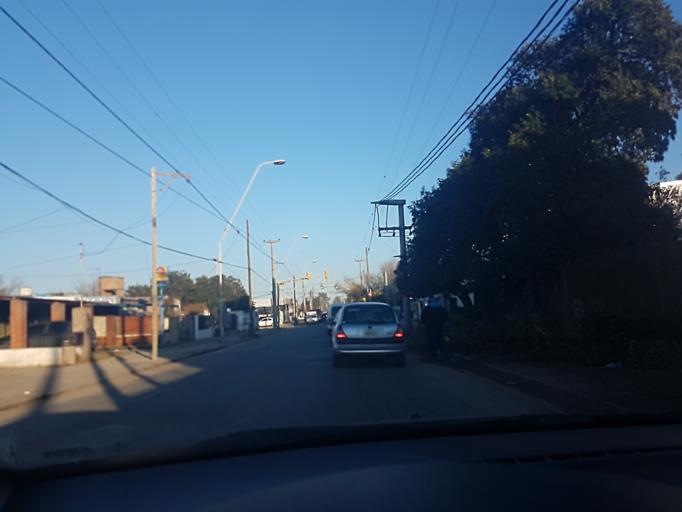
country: AR
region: Cordoba
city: Villa Allende
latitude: -31.3433
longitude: -64.2412
